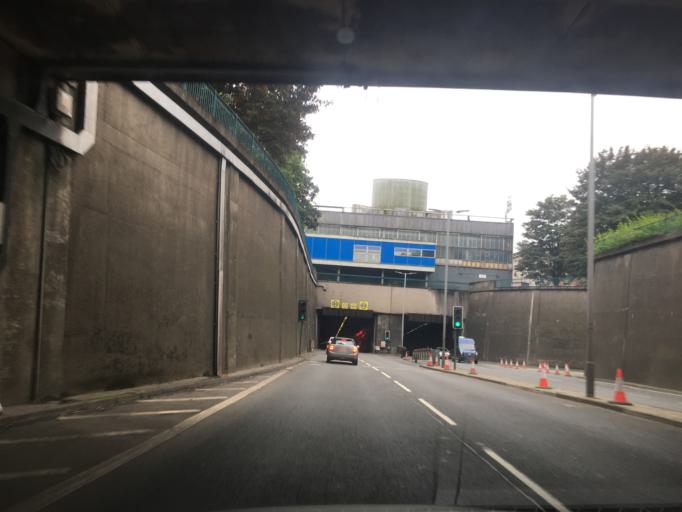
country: GB
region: Scotland
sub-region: East Dunbartonshire
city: Bearsden
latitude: 55.8726
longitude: -4.3294
